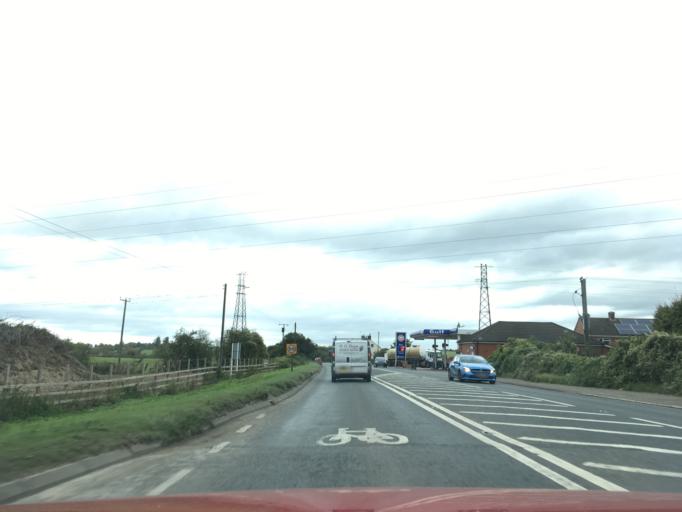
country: GB
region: England
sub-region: Gloucestershire
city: Stonehouse
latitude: 51.7581
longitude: -2.3375
